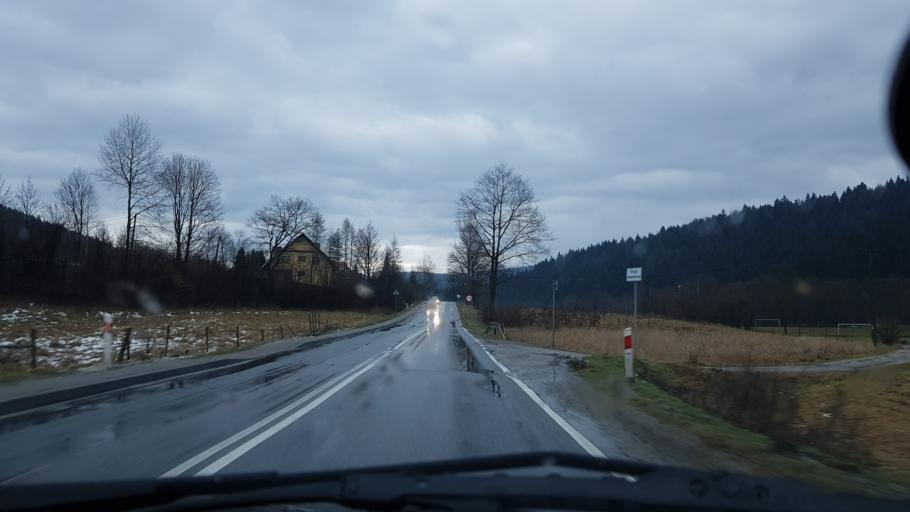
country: PL
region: Lesser Poland Voivodeship
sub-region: Powiat suski
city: Kukow
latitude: 49.7398
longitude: 19.4628
